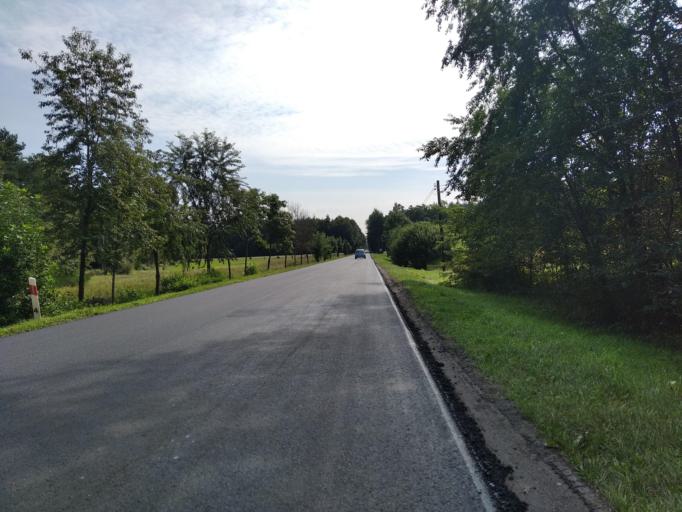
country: PL
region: Subcarpathian Voivodeship
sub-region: Powiat ropczycko-sedziszowski
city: Ostrow
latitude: 50.1546
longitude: 21.5604
